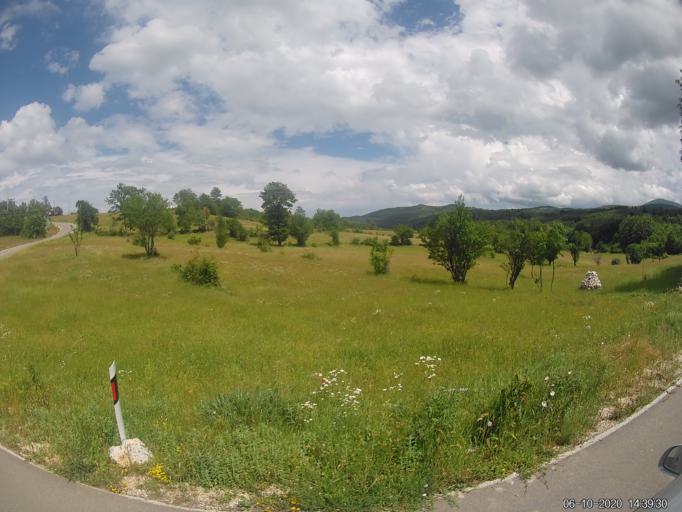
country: XK
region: Prizren
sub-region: Komuna e Therandes
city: Budakovo
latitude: 42.4002
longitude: 20.9457
